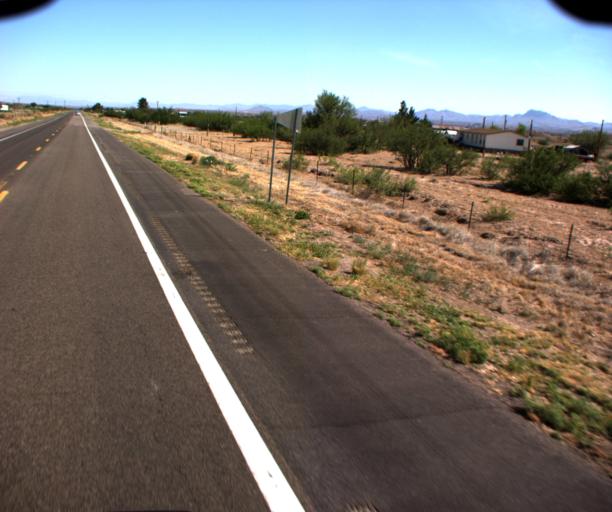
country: US
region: Arizona
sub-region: Greenlee County
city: Clifton
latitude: 32.6659
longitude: -109.0740
